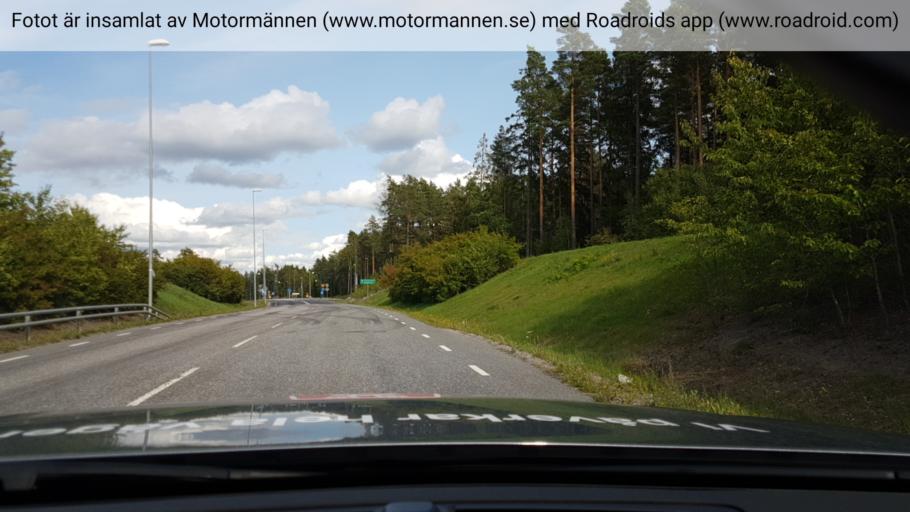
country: SE
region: Stockholm
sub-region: Upplands-Bro Kommun
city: Bro
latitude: 59.5085
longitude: 17.6666
